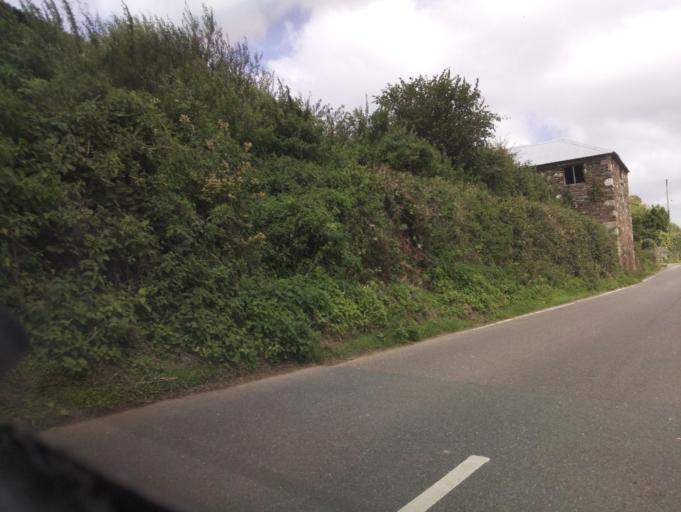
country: GB
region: England
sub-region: Devon
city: South Brent
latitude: 50.4060
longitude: -3.8216
